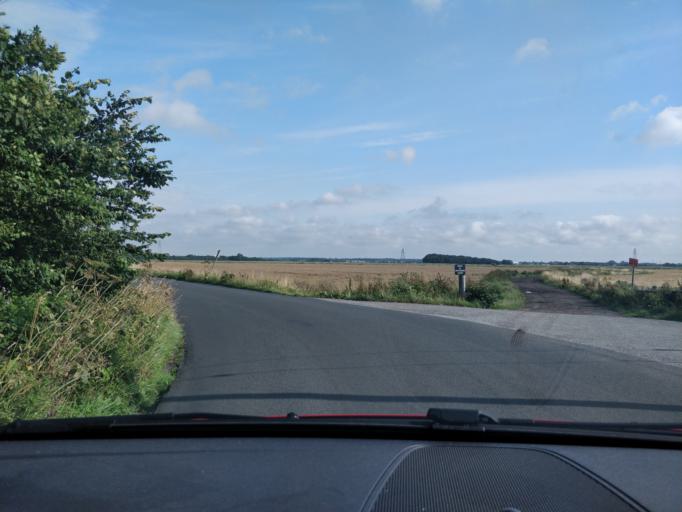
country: GB
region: England
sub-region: Lancashire
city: Banks
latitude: 53.6509
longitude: -2.9486
